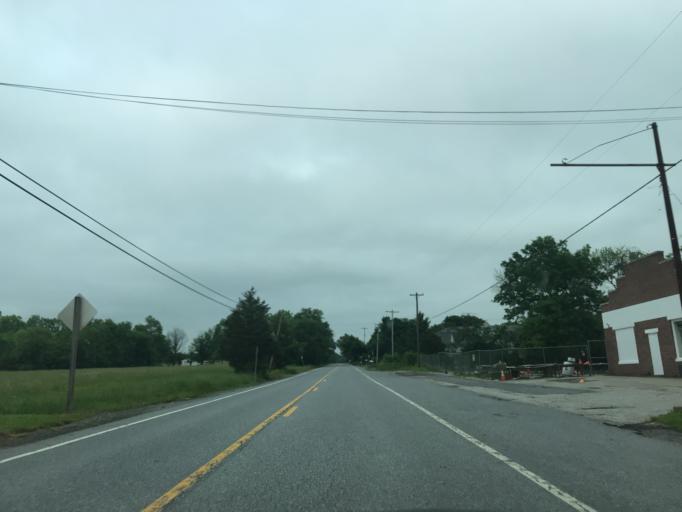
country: US
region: Maryland
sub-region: Frederick County
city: Emmitsburg
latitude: 39.7088
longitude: -77.3209
